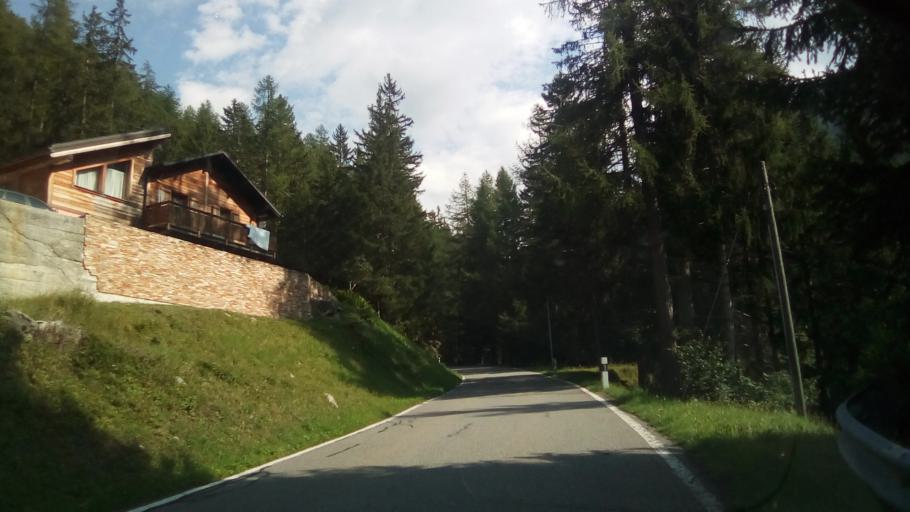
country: CH
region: Valais
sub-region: Martigny District
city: Martigny-Combe
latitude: 46.0533
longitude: 7.0843
